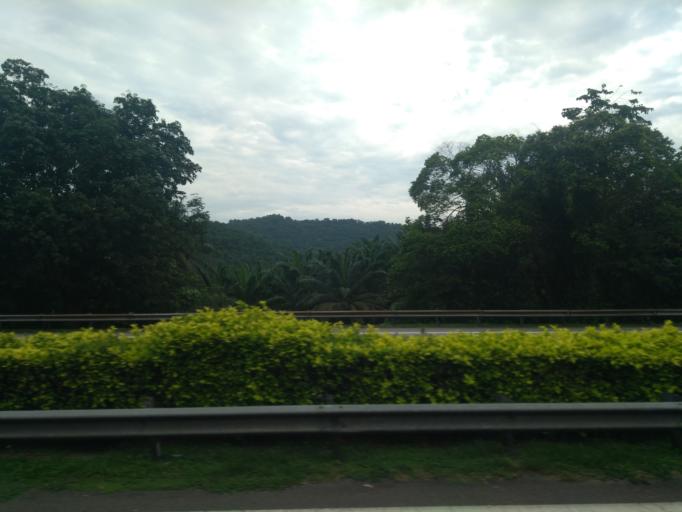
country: MY
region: Negeri Sembilan
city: Tampin
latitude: 2.4574
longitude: 102.1640
